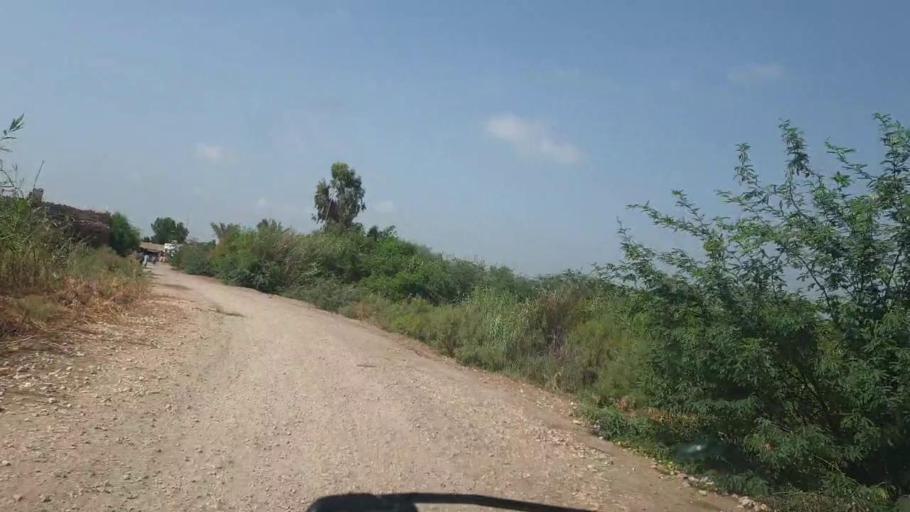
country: PK
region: Sindh
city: Berani
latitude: 25.7408
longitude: 68.9544
